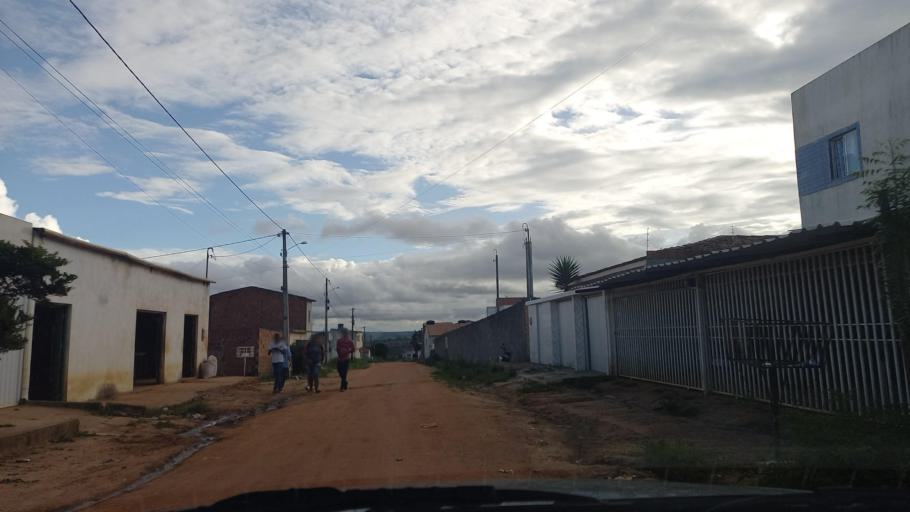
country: BR
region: Pernambuco
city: Garanhuns
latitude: -8.9150
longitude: -36.4795
